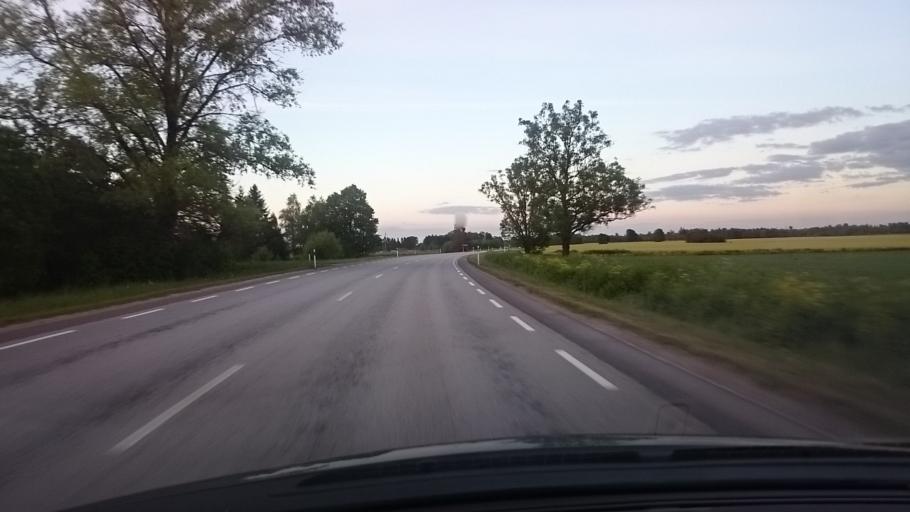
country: EE
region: Viljandimaa
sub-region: Vohma linn
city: Vohma
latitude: 58.6527
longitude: 25.5919
